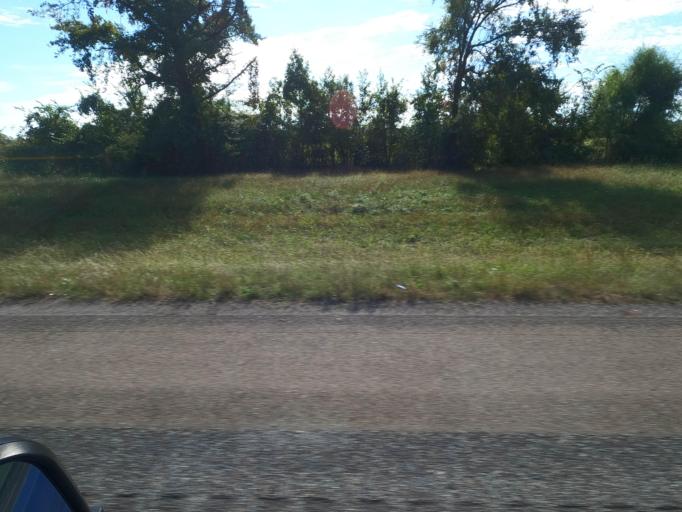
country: US
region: Tennessee
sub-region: Madison County
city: Jackson
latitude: 35.6391
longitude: -88.9281
